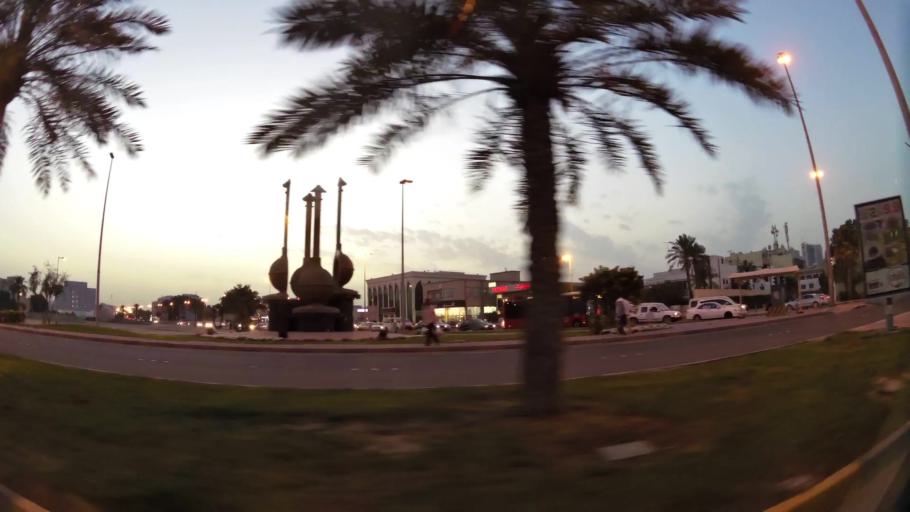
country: BH
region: Manama
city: Jidd Hafs
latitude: 26.2163
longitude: 50.5653
